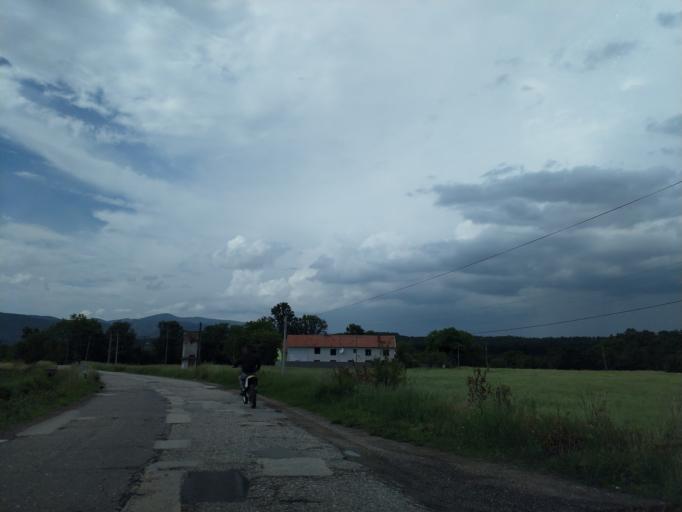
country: RS
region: Central Serbia
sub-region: Zajecarski Okrug
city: Boljevac
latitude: 43.8921
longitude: 21.9669
